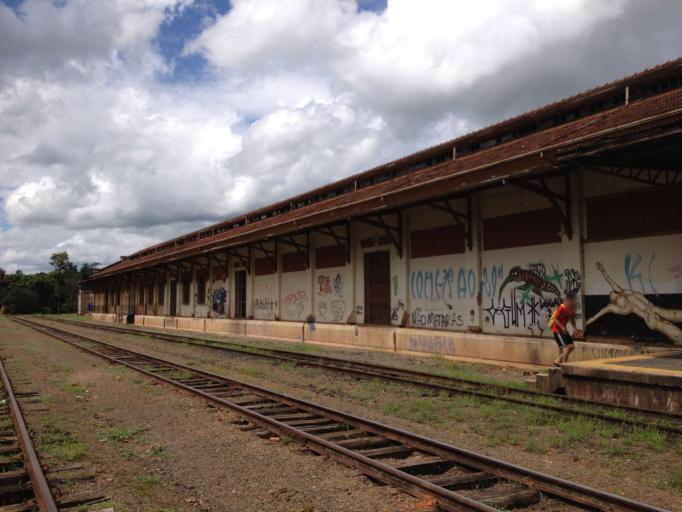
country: BR
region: Sao Paulo
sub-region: Sao Joao Da Boa Vista
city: Sao Joao da Boa Vista
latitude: -21.9650
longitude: -46.8007
